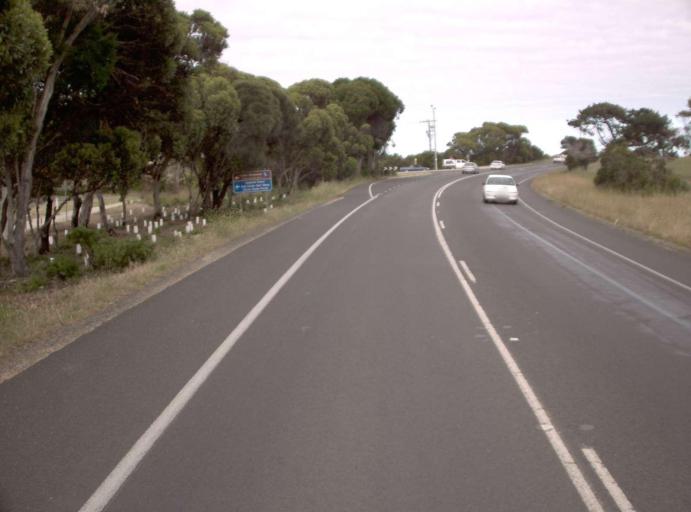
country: AU
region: Victoria
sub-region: Bass Coast
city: Phillip Island
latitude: -38.5209
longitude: 145.3358
